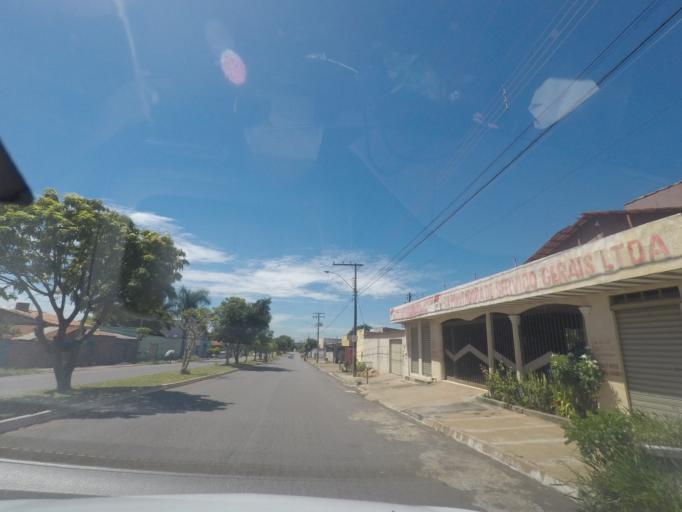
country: BR
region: Goias
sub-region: Aparecida De Goiania
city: Aparecida de Goiania
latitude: -16.7725
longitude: -49.3422
